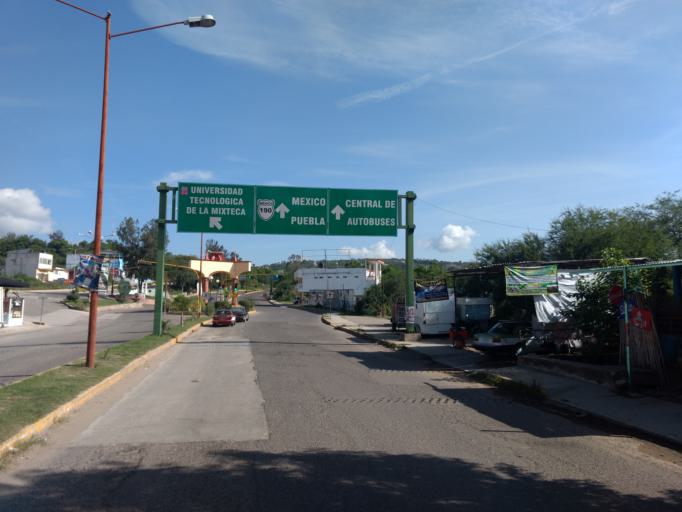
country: MX
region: Oaxaca
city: Ciudad de Huajuapam de Leon
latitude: 17.8174
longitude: -97.7908
